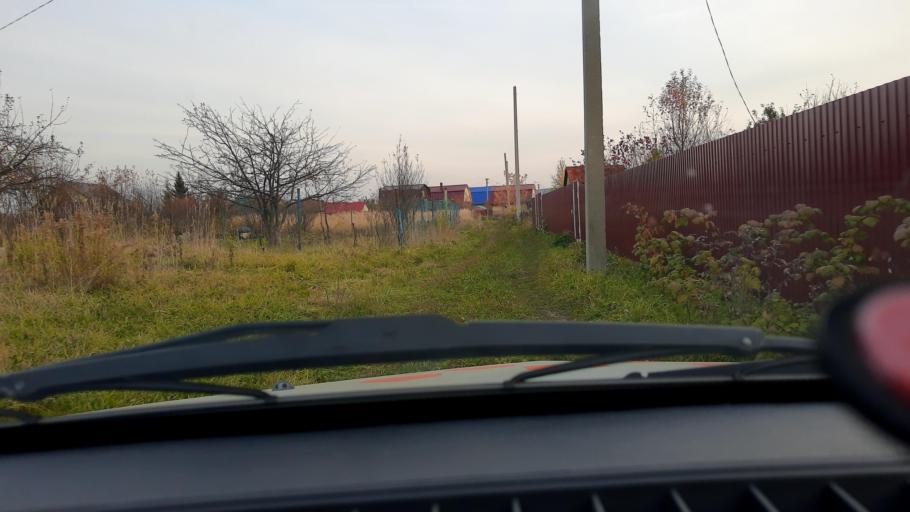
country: RU
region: Bashkortostan
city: Iglino
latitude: 54.8042
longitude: 56.3500
